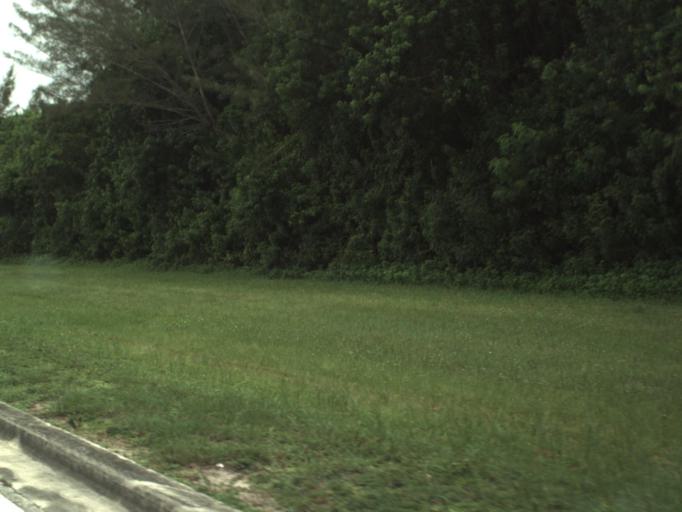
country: US
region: Florida
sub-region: Palm Beach County
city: Boca Pointe
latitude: 26.3496
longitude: -80.1800
